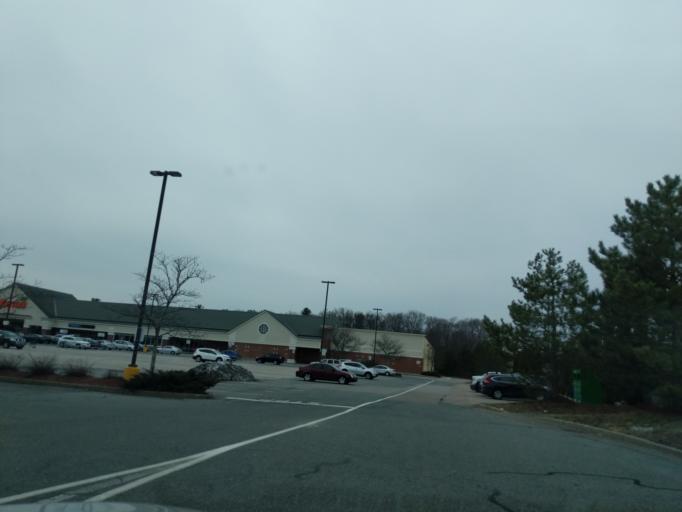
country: US
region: Massachusetts
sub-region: Bristol County
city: Attleboro
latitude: 41.9715
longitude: -71.2994
